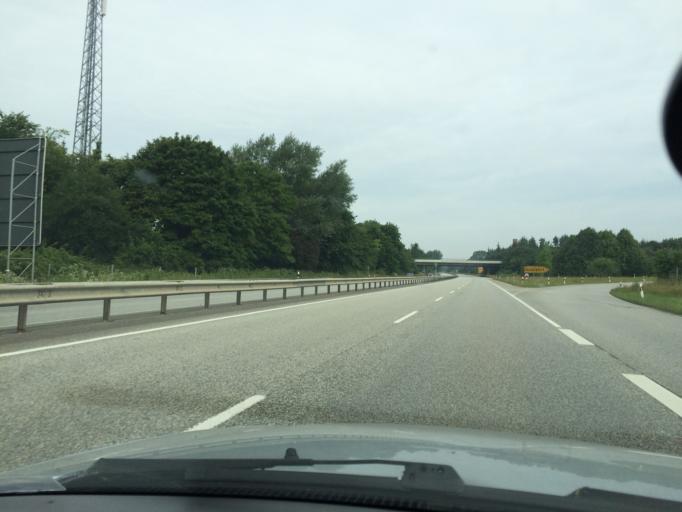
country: DE
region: Schleswig-Holstein
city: Flensburg
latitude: 54.7663
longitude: 9.4246
